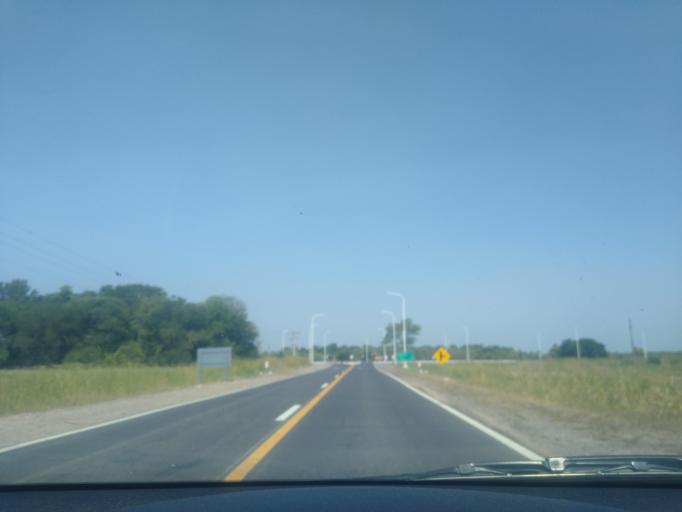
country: AR
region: Chaco
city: Fontana
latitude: -27.5769
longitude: -59.1600
